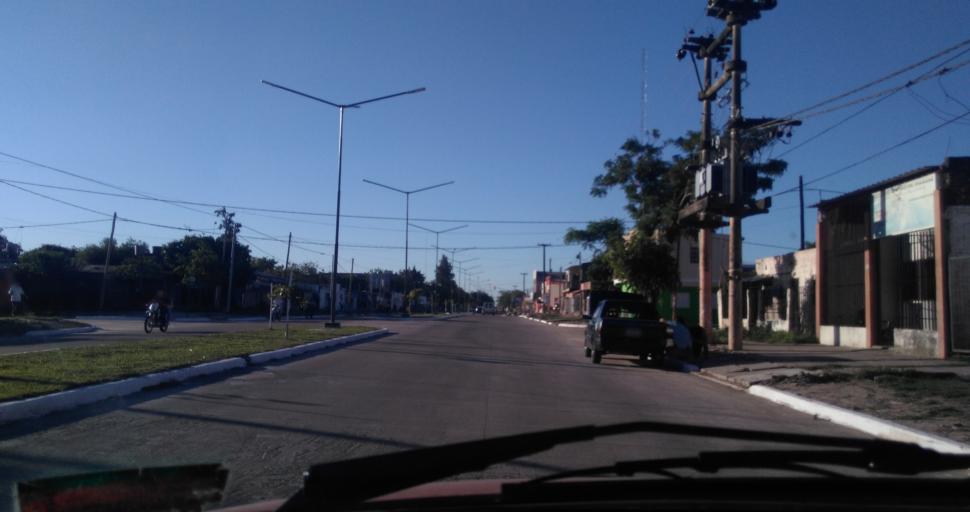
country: AR
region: Chaco
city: Resistencia
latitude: -27.4780
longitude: -58.9848
